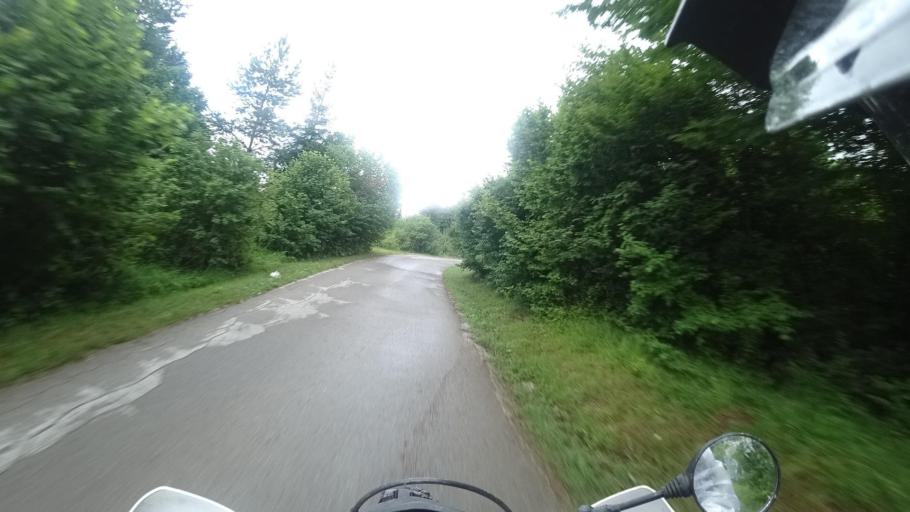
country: HR
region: Karlovacka
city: Plaski
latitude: 45.0023
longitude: 15.4204
